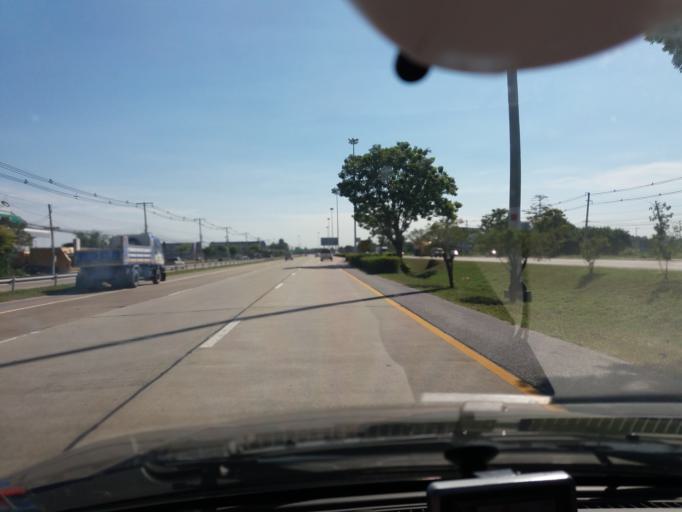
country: TH
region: Suphan Buri
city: Suphan Buri
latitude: 14.4529
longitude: 100.1314
